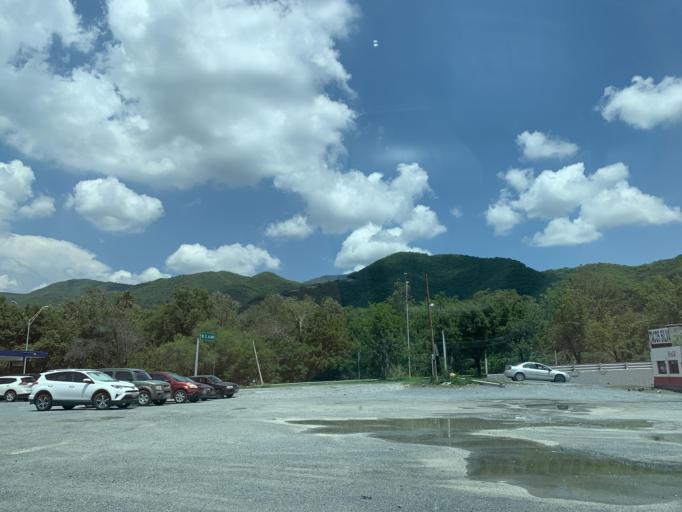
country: MX
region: Nuevo Leon
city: Santiago
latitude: 25.3754
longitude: -100.1106
